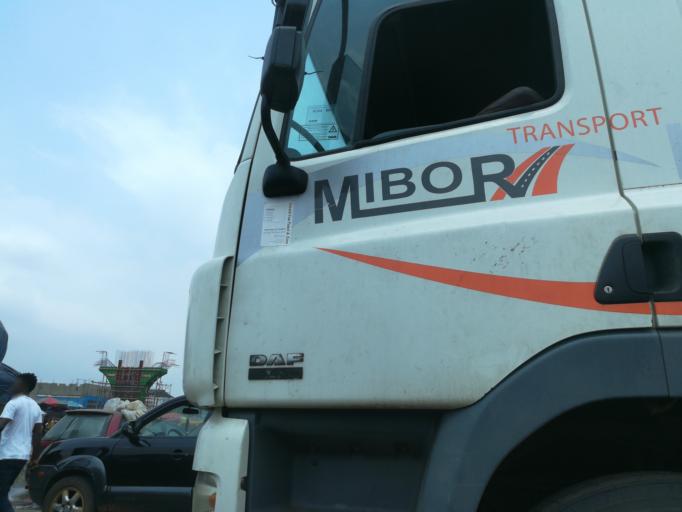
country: NG
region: Lagos
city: Agege
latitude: 6.6269
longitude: 3.3227
